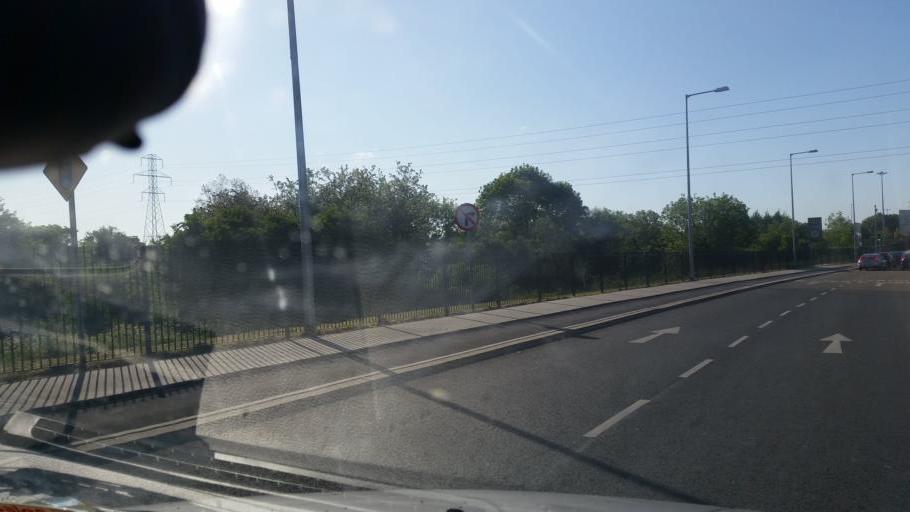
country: IE
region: Leinster
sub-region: Fingal County
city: Blanchardstown
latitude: 53.3997
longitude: -6.3922
